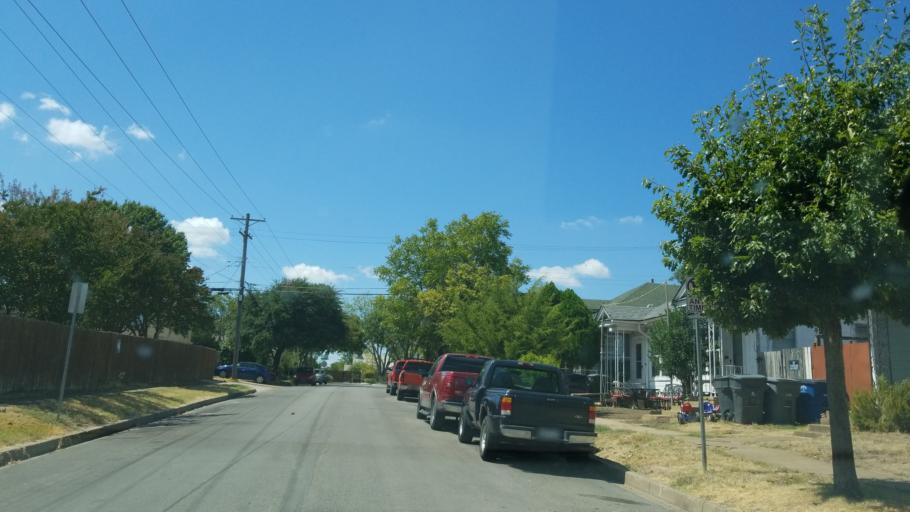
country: US
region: Texas
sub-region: Dallas County
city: Dallas
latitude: 32.7561
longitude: -96.8303
